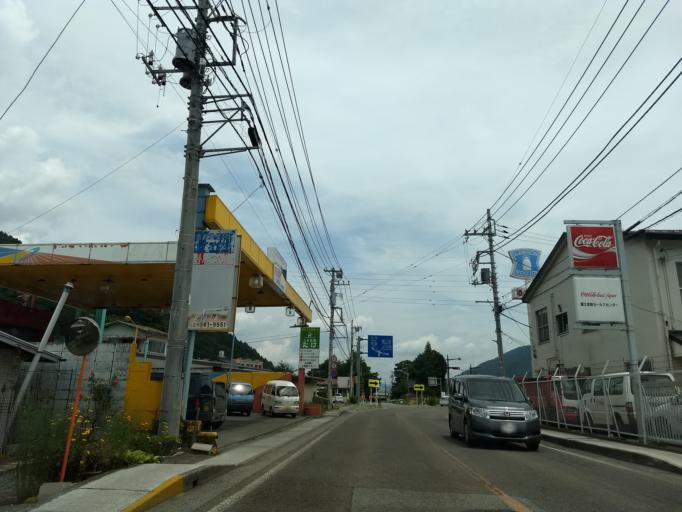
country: JP
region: Yamanashi
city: Fujikawaguchiko
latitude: 35.5031
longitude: 138.8178
